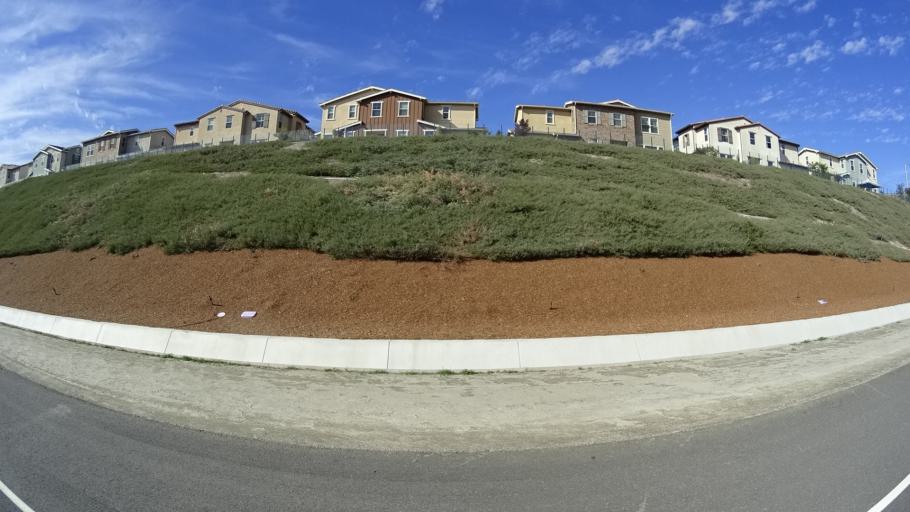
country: US
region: California
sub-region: Orange County
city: Ladera Ranch
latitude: 33.5457
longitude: -117.5935
